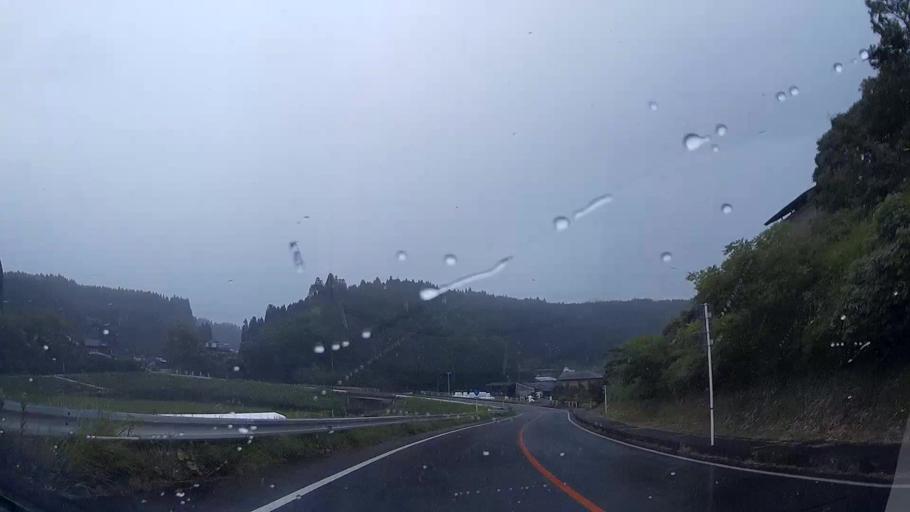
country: JP
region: Oita
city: Tsukawaki
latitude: 33.1297
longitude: 131.0863
